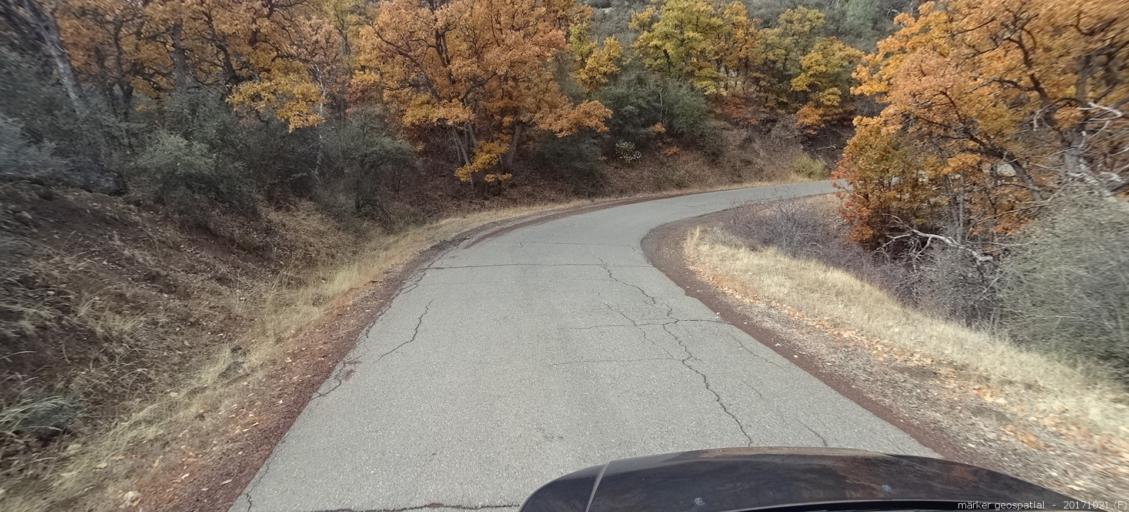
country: US
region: California
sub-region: Shasta County
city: Burney
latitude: 40.9608
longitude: -121.5543
